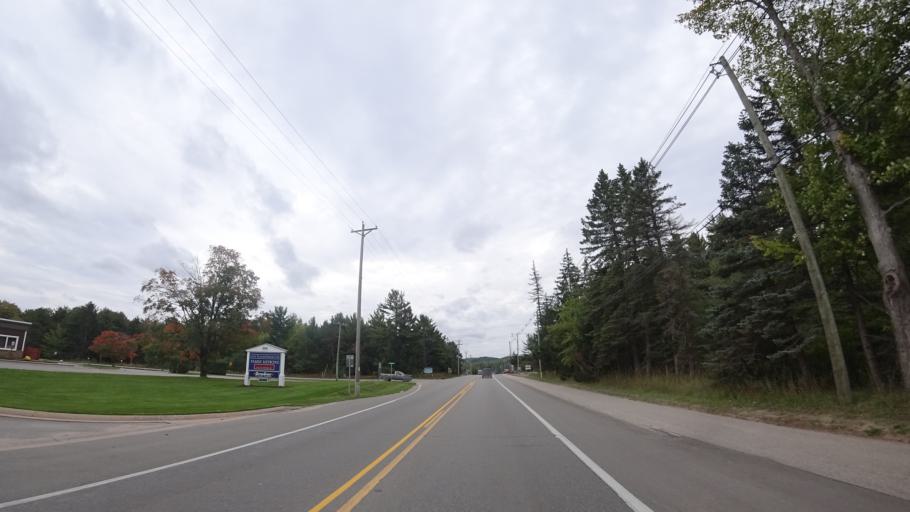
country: US
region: Michigan
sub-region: Emmet County
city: Petoskey
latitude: 45.4225
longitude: -84.9045
